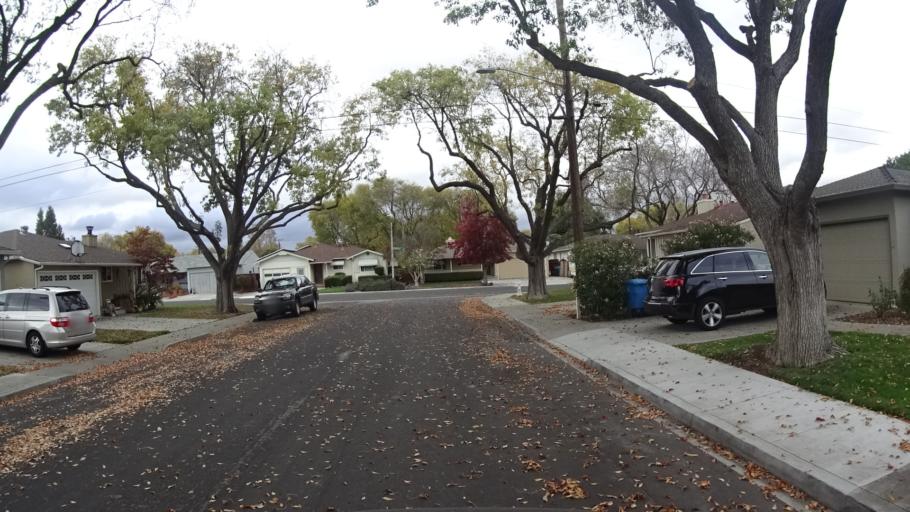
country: US
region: California
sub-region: Santa Clara County
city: Santa Clara
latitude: 37.3343
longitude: -121.9731
